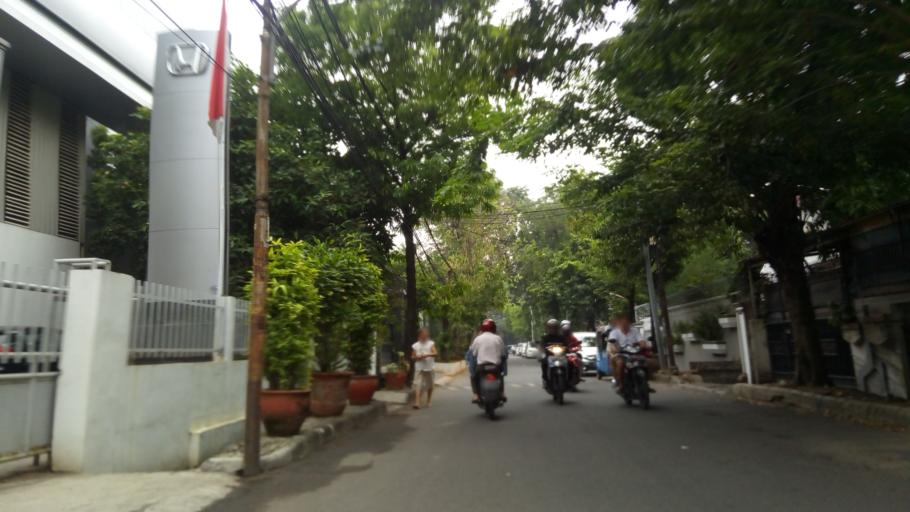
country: ID
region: Jakarta Raya
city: Jakarta
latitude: -6.1440
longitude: 106.8396
